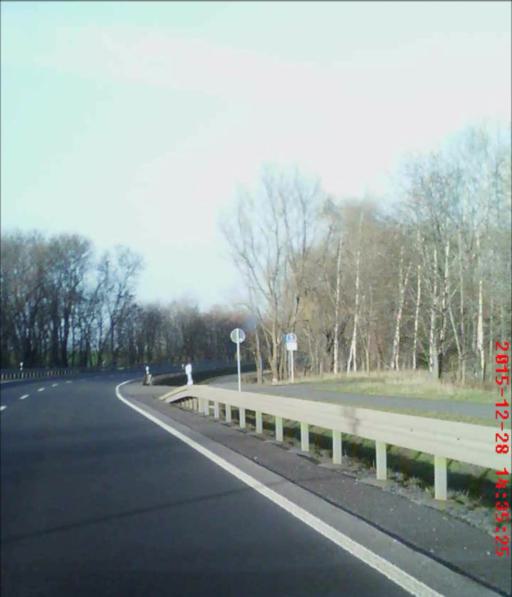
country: DE
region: Thuringia
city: Grossobringen
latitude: 51.0409
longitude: 11.3363
